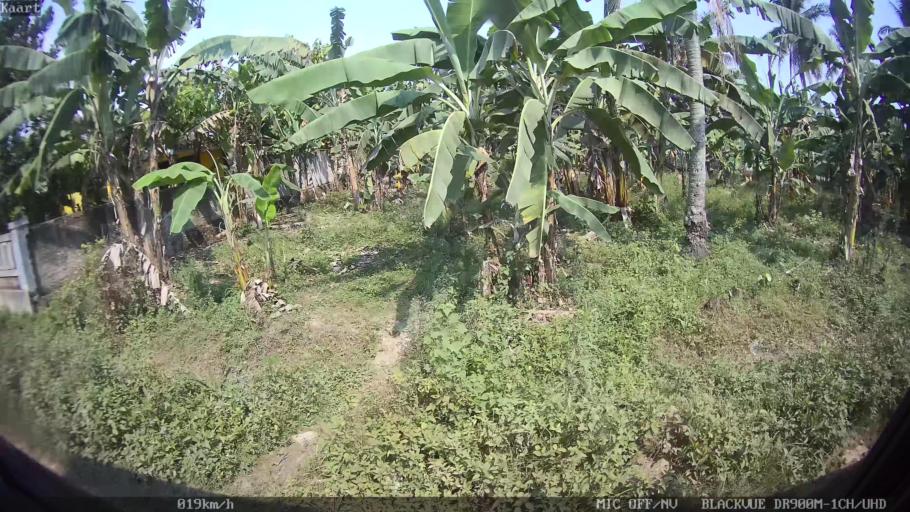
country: ID
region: Lampung
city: Natar
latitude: -5.2972
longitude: 105.2259
